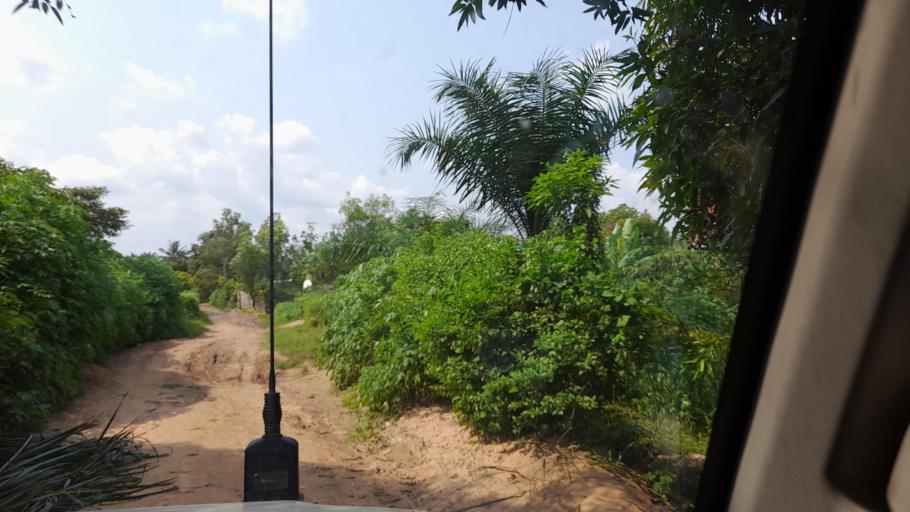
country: CD
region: Kasai-Occidental
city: Kananga
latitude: -5.9080
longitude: 22.4757
